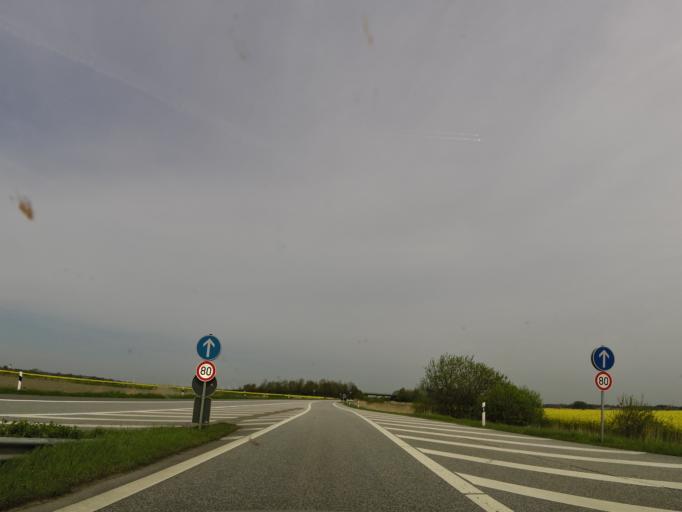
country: DE
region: Schleswig-Holstein
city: Lohe-Rickelshof
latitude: 54.1963
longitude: 9.0452
